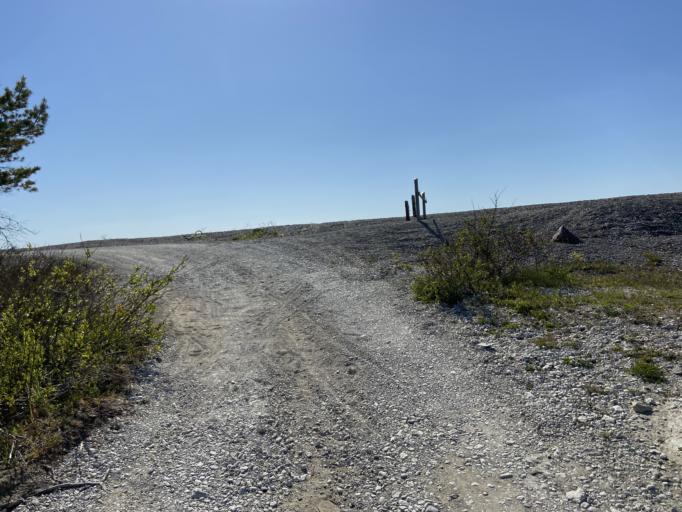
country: EE
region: Harju
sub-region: Paldiski linn
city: Paldiski
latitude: 59.2697
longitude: 23.7322
